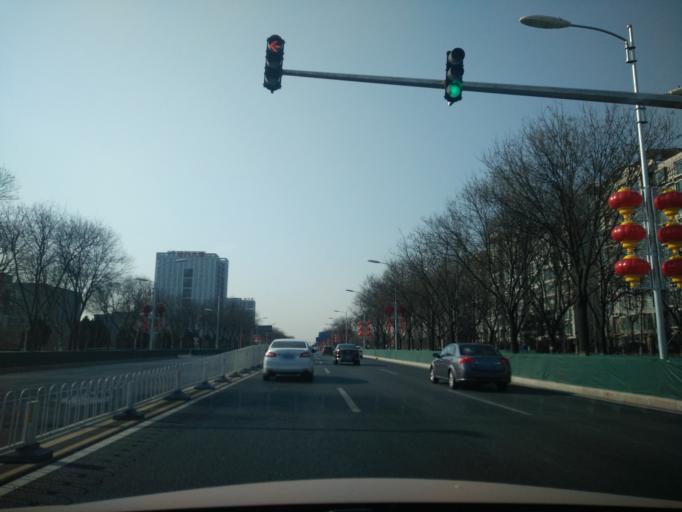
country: CN
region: Beijing
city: Jiugong
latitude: 39.7875
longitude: 116.4952
